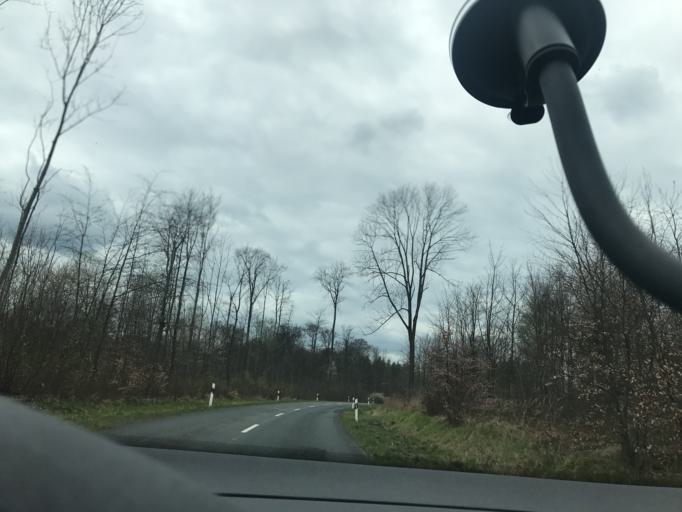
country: DE
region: Lower Saxony
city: Rabke
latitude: 52.1652
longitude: 10.8872
